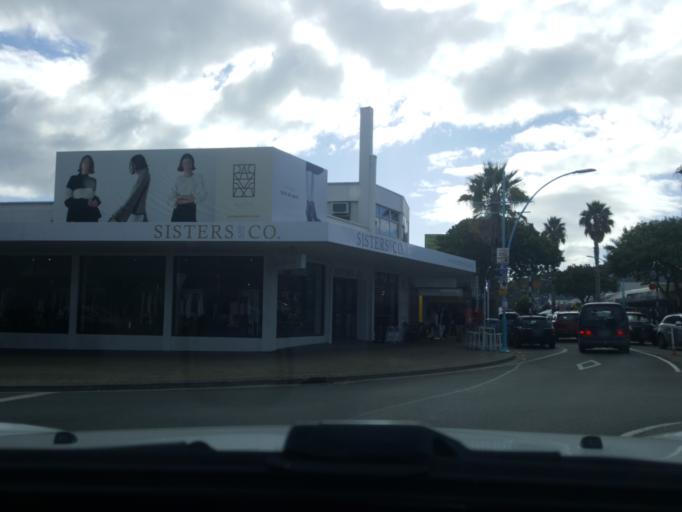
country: NZ
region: Bay of Plenty
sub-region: Tauranga City
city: Tauranga
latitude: -37.6398
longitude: 176.1841
